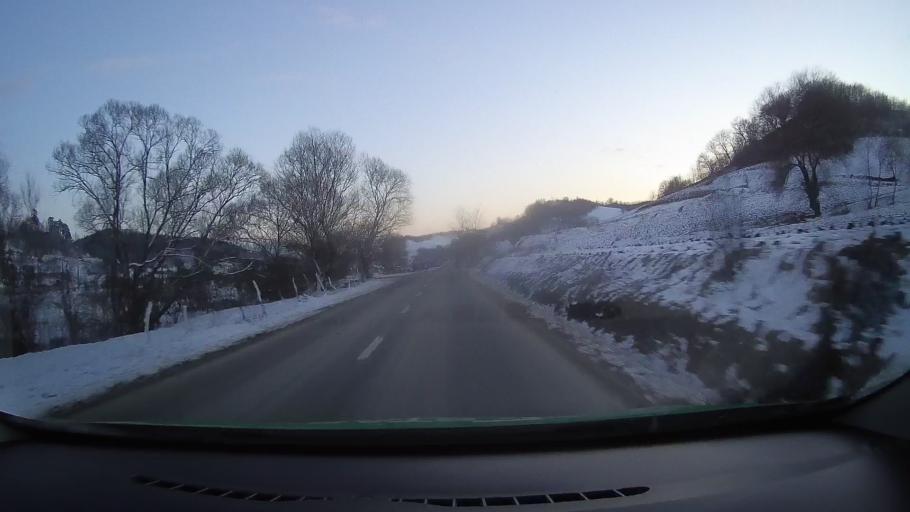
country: RO
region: Sibiu
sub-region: Comuna Alma
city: Alma
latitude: 46.2036
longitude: 24.4582
